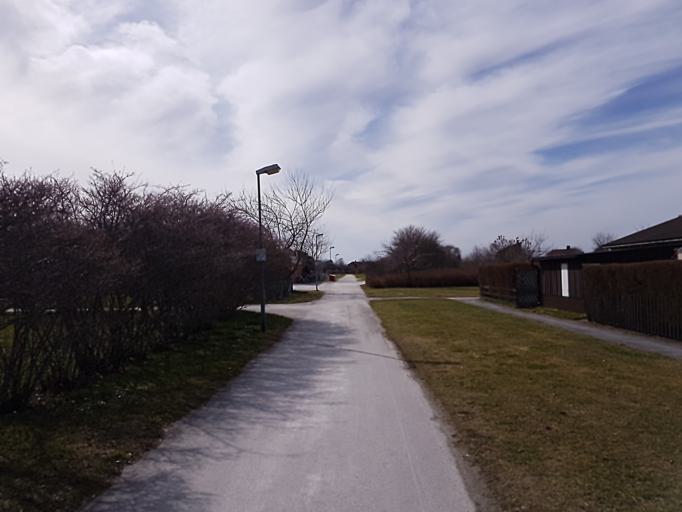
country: SE
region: Gotland
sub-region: Gotland
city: Visby
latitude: 57.6317
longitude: 18.3211
